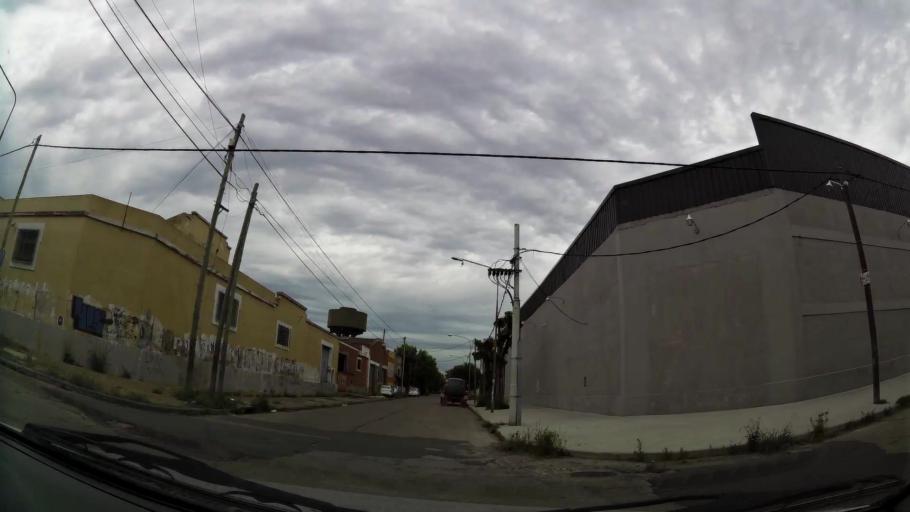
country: AR
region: Buenos Aires
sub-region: Partido de Lanus
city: Lanus
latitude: -34.6895
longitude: -58.3911
